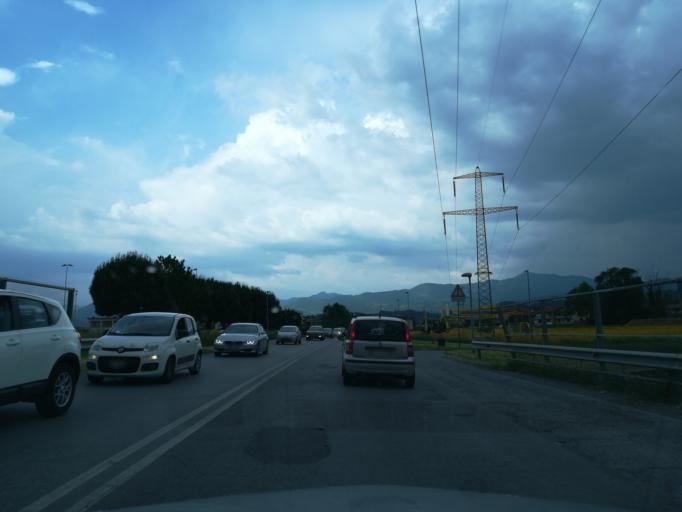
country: IT
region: Lombardy
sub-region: Provincia di Bergamo
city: Mozzo
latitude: 45.7066
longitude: 9.6062
